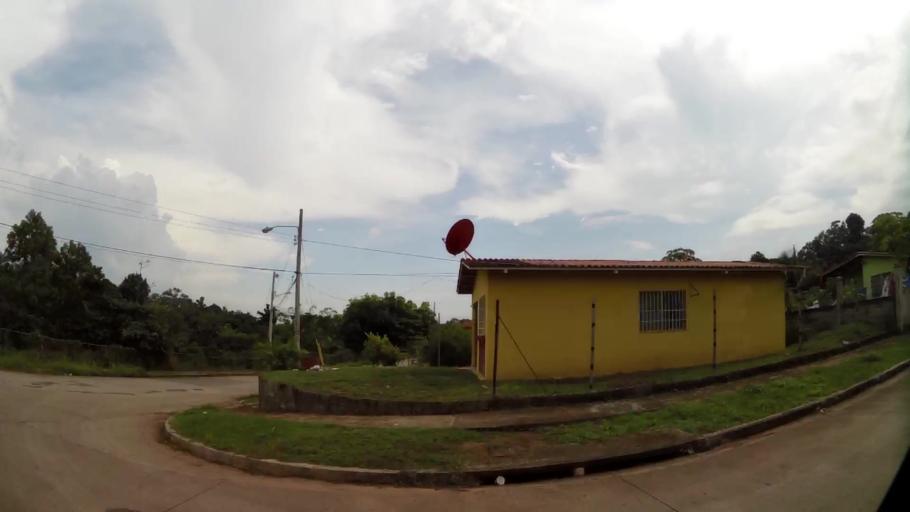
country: PA
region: Panama
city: Tocumen
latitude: 9.1100
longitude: -79.3782
